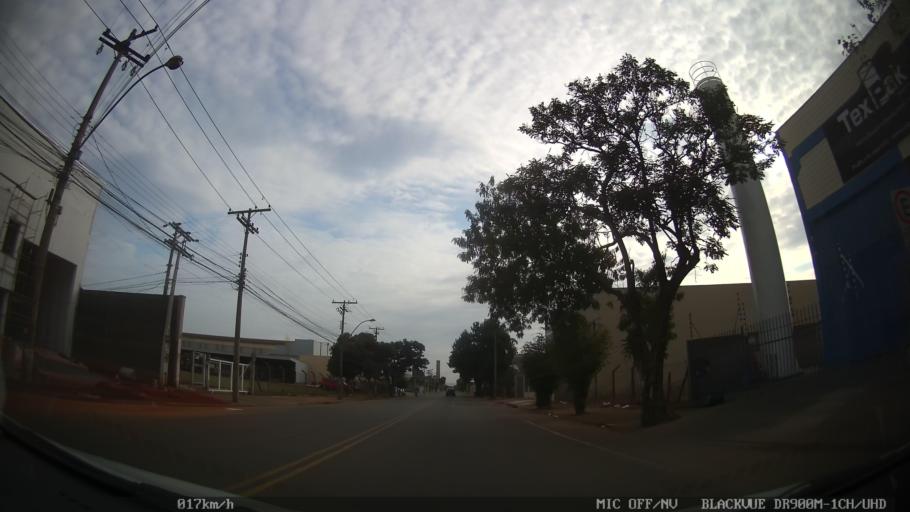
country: BR
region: Sao Paulo
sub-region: Santa Barbara D'Oeste
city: Santa Barbara d'Oeste
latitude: -22.7606
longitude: -47.3861
